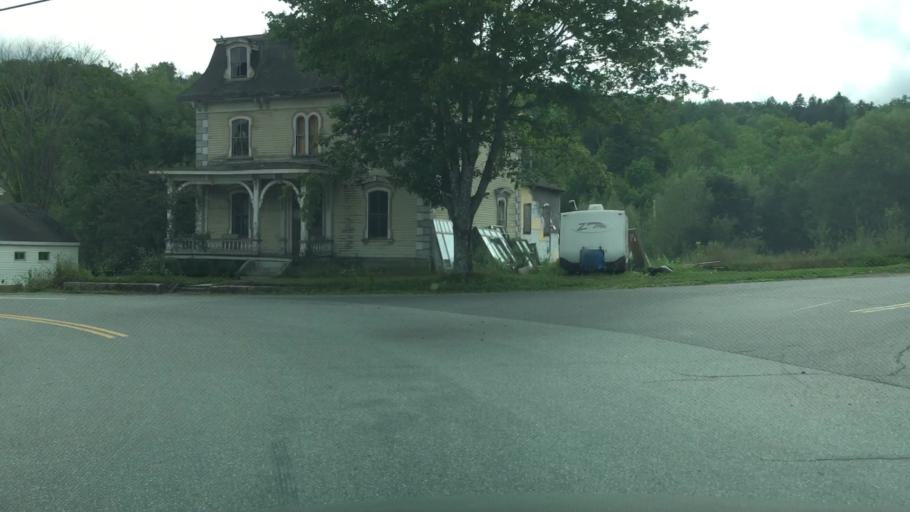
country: US
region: Maine
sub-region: Waldo County
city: Frankfort
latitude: 44.6088
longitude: -68.8744
